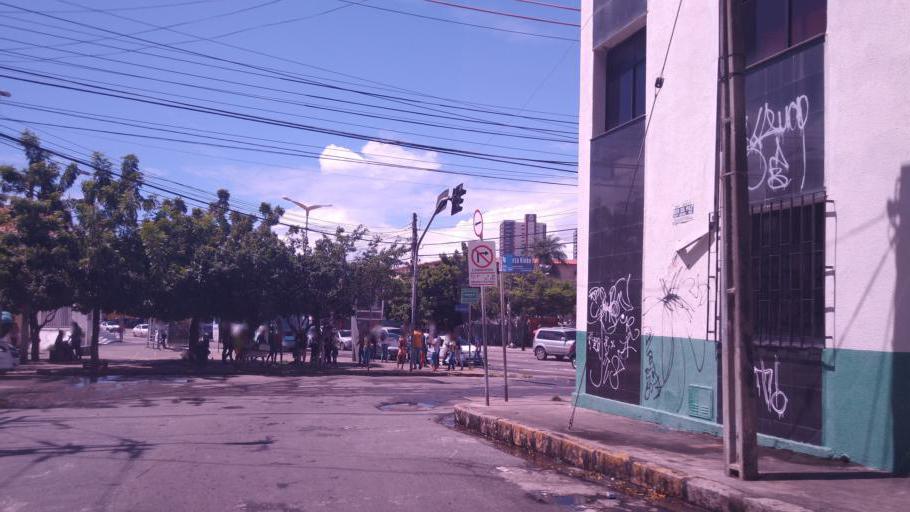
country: BR
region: Ceara
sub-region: Fortaleza
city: Fortaleza
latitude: -3.7253
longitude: -38.4849
